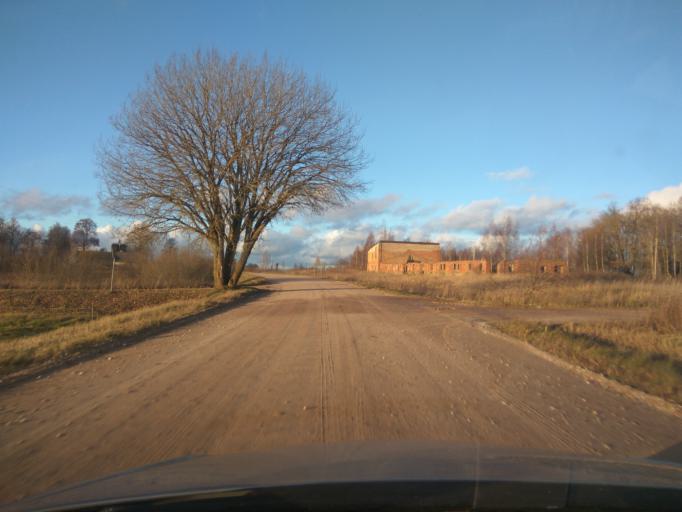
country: LV
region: Aizpute
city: Aizpute
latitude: 56.7957
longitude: 21.7916
